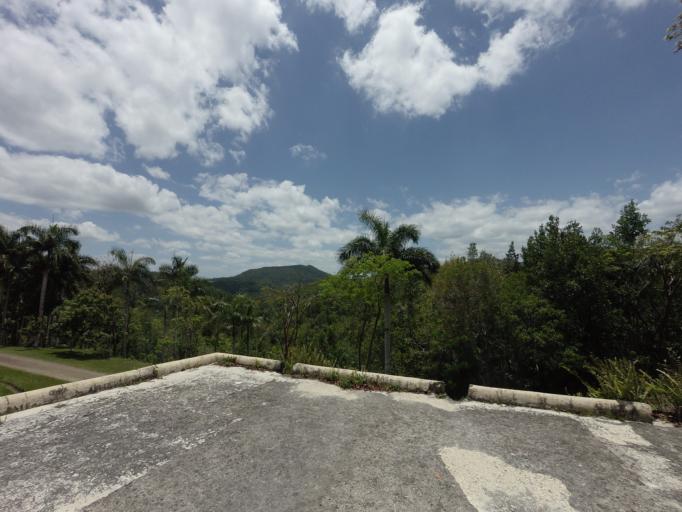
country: CU
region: Artemisa
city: Soroa
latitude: 22.8625
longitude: -82.9283
